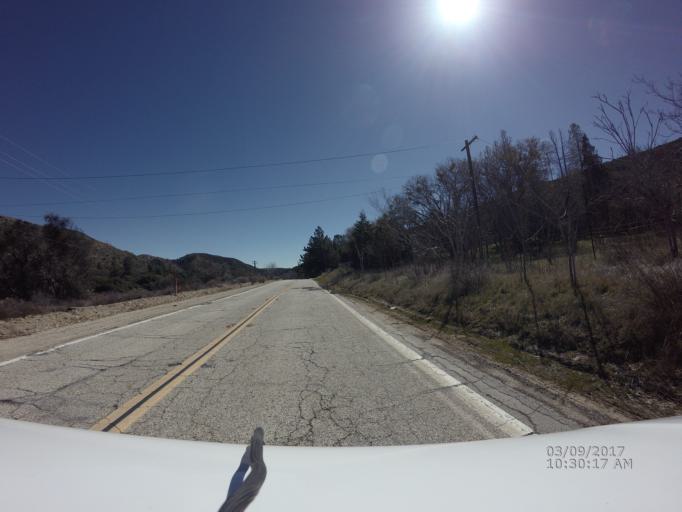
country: US
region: California
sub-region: Los Angeles County
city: Green Valley
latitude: 34.6913
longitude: -118.4860
